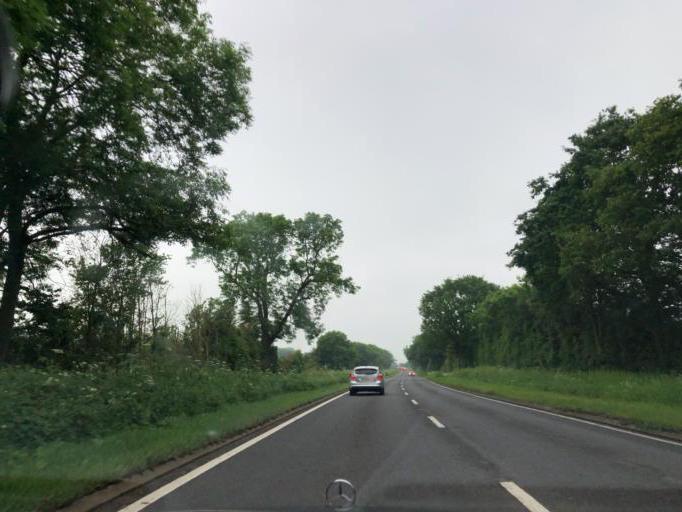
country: GB
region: England
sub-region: Warwickshire
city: Harbury
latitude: 52.2154
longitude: -1.5135
